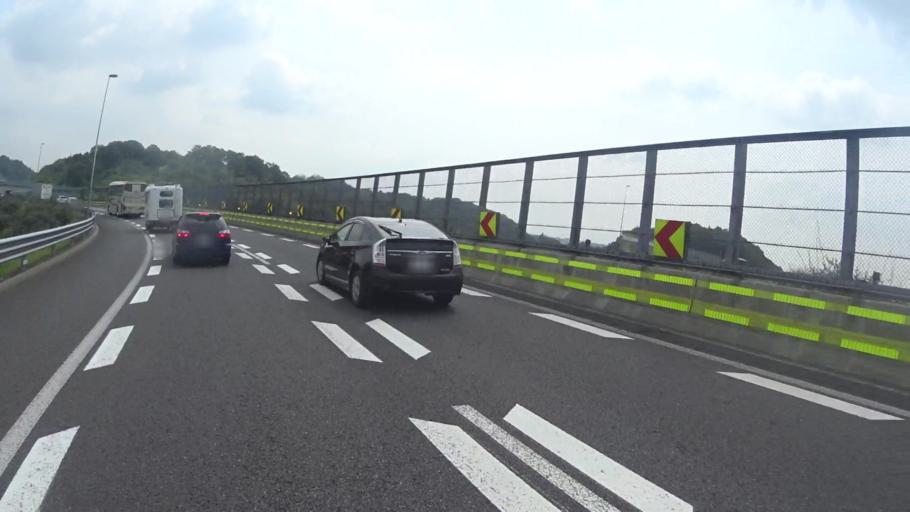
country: JP
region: Mie
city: Kameyama
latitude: 34.8973
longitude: 136.4546
